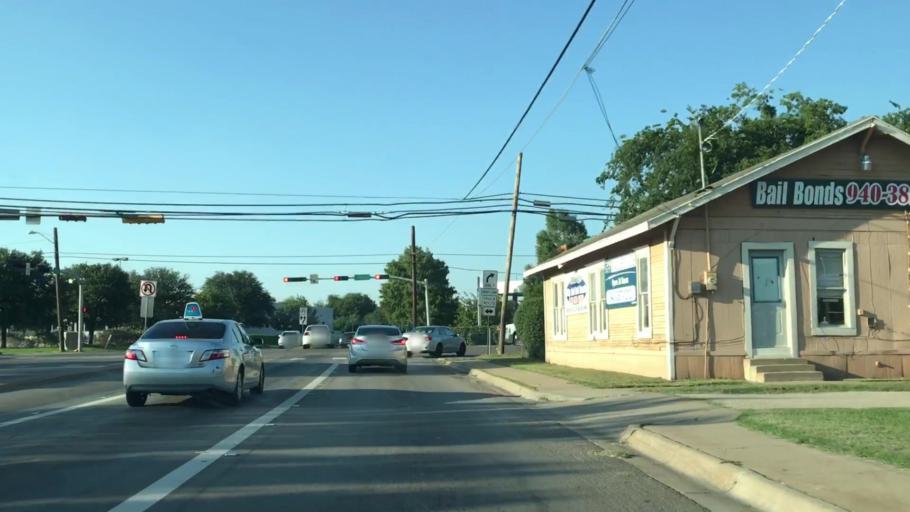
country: US
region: Texas
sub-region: Denton County
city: Denton
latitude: 33.2153
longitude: -97.1119
